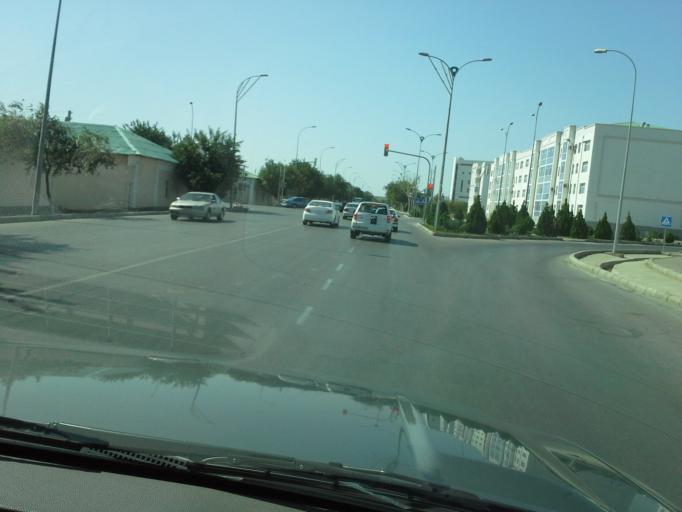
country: TM
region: Dasoguz
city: Dasoguz
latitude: 41.8387
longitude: 59.9502
